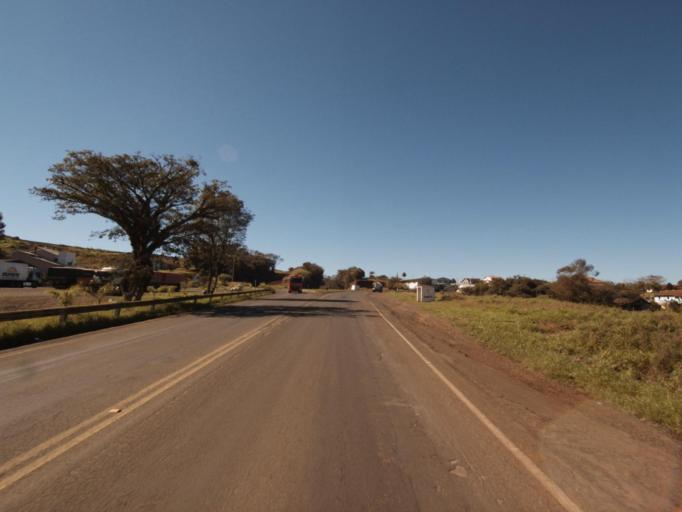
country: BR
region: Santa Catarina
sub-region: Sao Lourenco Do Oeste
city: Sao Lourenco dOeste
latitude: -26.8258
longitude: -53.0934
